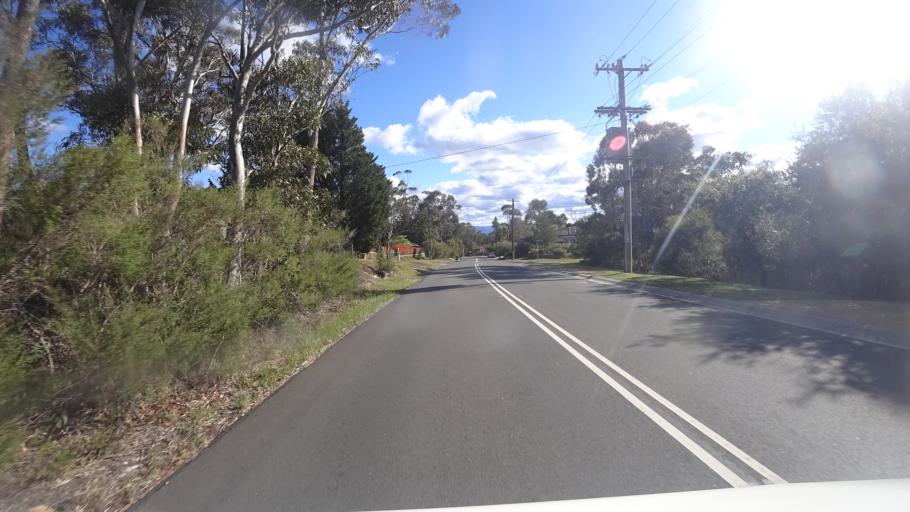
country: AU
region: New South Wales
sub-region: Blue Mountains Municipality
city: Katoomba
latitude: -33.7179
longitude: 150.2950
